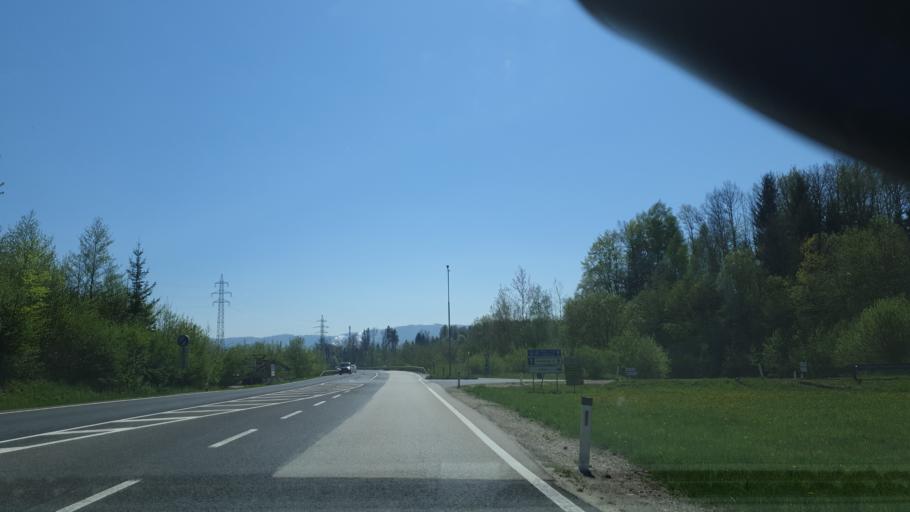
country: AT
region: Upper Austria
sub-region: Politischer Bezirk Vocklabruck
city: Timelkam
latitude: 47.9976
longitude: 13.5968
